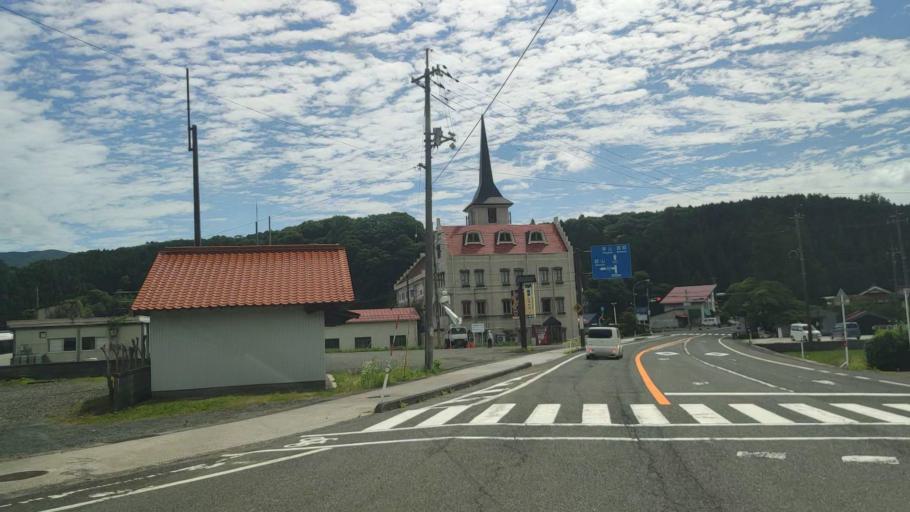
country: JP
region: Okayama
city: Niimi
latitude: 35.1792
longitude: 133.5668
